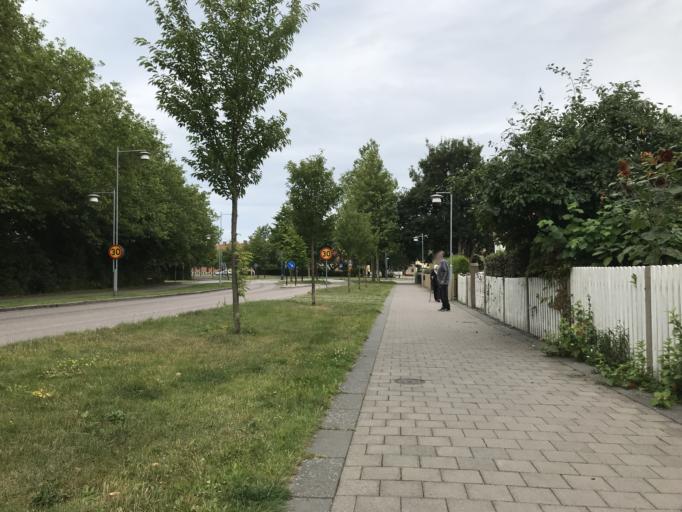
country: SE
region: Skane
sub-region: Landskrona
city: Landskrona
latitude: 55.8800
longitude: 12.8390
